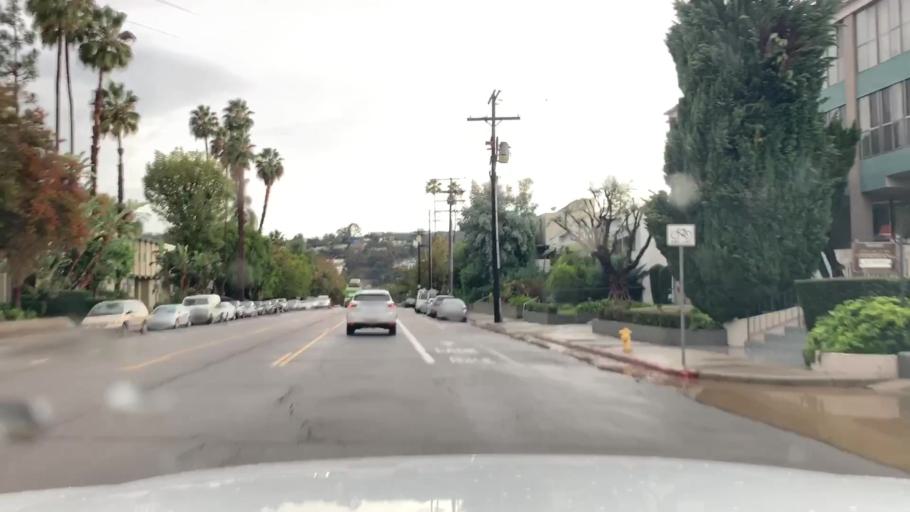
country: US
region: California
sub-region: Los Angeles County
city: North Hollywood
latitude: 34.1486
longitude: -118.3877
